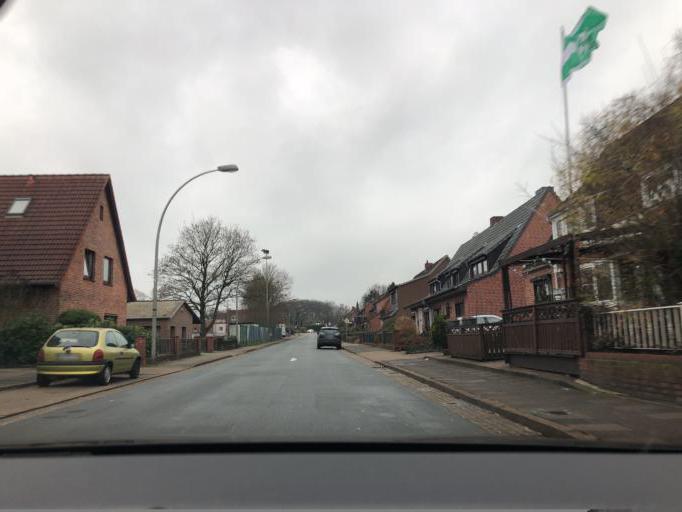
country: DE
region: Lower Saxony
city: Ritterhude
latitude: 53.1872
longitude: 8.7501
